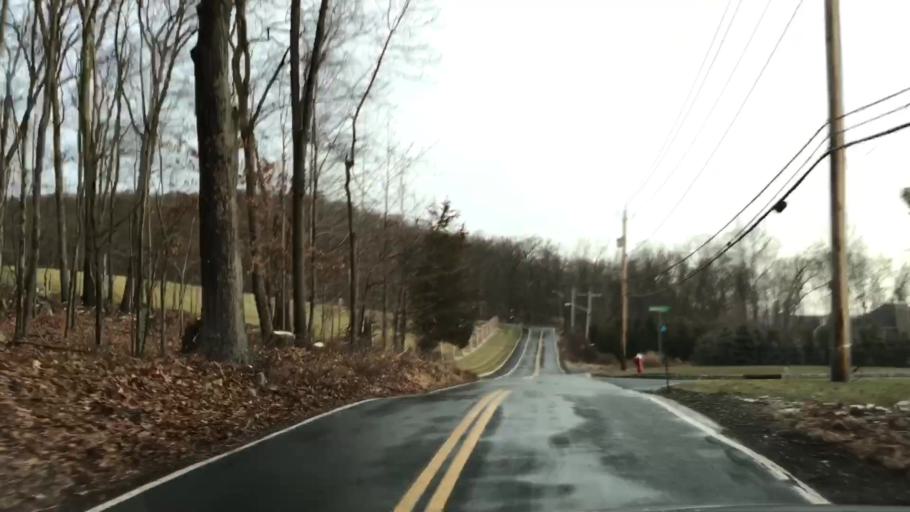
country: US
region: New York
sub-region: Rockland County
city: Thiells
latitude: 41.2297
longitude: -74.0450
